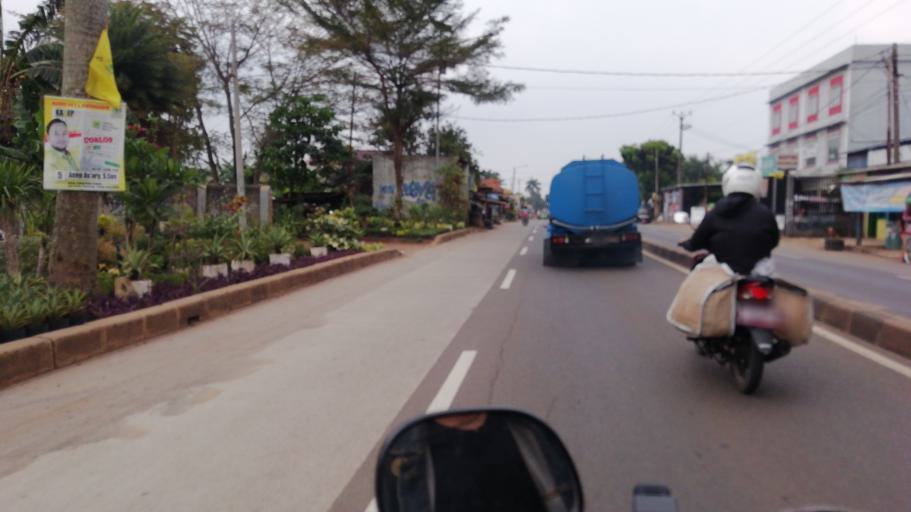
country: ID
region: West Java
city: Parung
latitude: -6.4556
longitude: 106.7309
